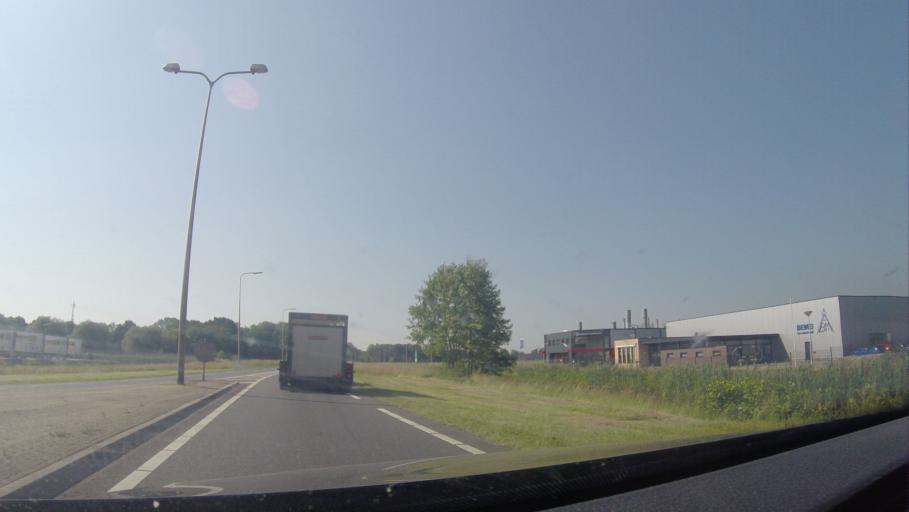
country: NL
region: Gelderland
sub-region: Gemeente Lochem
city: Laren
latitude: 52.2776
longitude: 6.4014
